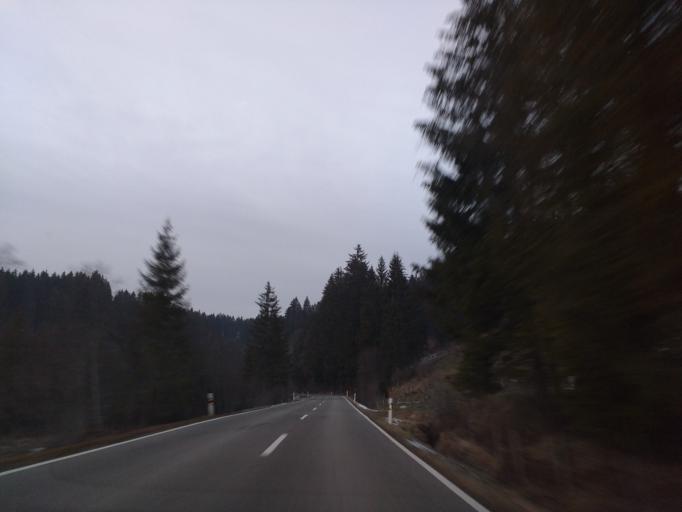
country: DE
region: Bavaria
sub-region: Swabia
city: Halblech
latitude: 47.6489
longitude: 10.7965
